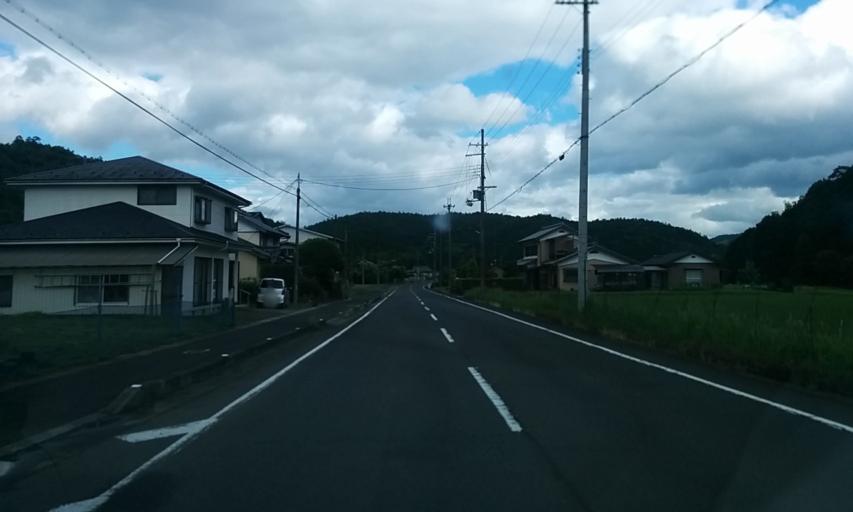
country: JP
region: Kyoto
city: Ayabe
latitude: 35.3744
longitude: 135.2369
